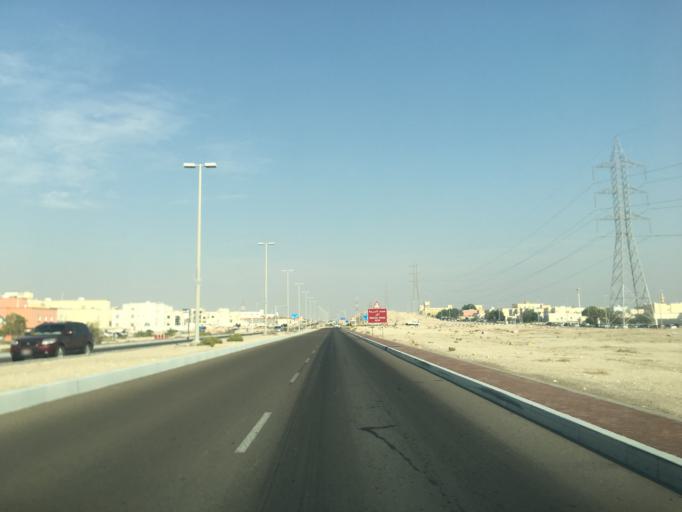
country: AE
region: Abu Dhabi
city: Abu Dhabi
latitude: 24.3019
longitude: 54.6543
